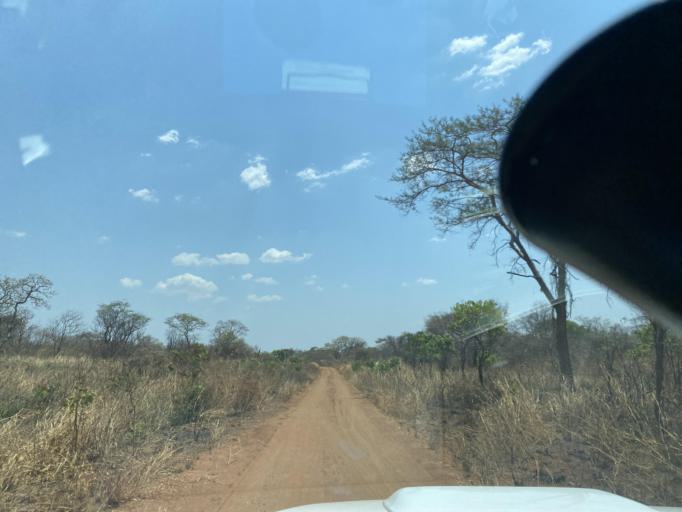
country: ZM
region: Lusaka
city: Lusaka
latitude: -15.5084
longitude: 28.0025
